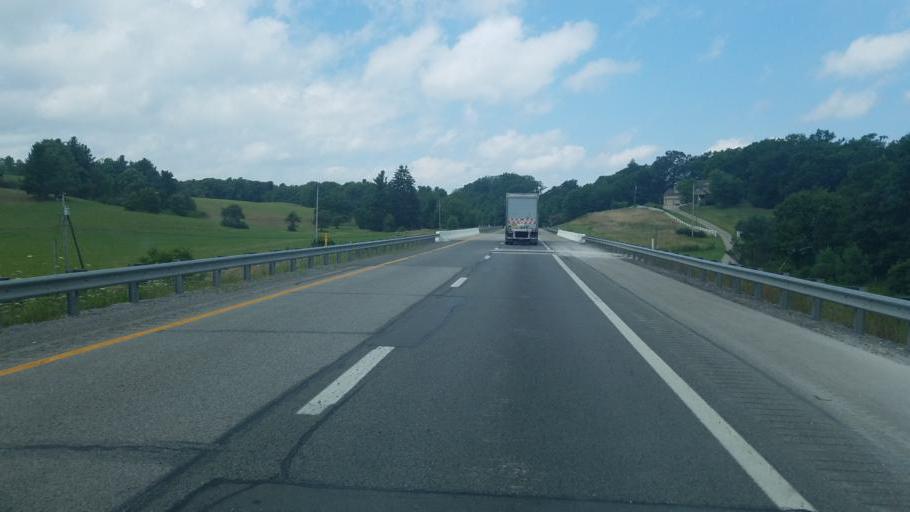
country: US
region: West Virginia
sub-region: Raleigh County
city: Shady Spring
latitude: 37.6494
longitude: -81.1086
